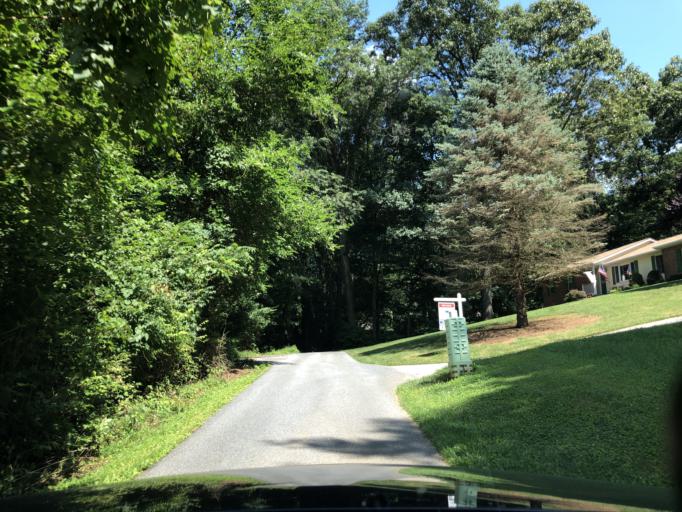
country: US
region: Maryland
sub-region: Carroll County
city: Westminster
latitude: 39.6213
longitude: -77.0025
